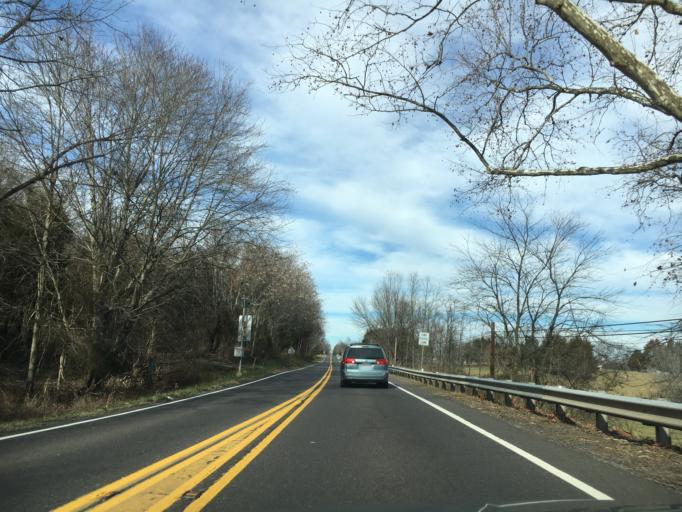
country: US
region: Virginia
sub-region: Culpeper County
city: Culpeper
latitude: 38.5509
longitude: -77.9786
